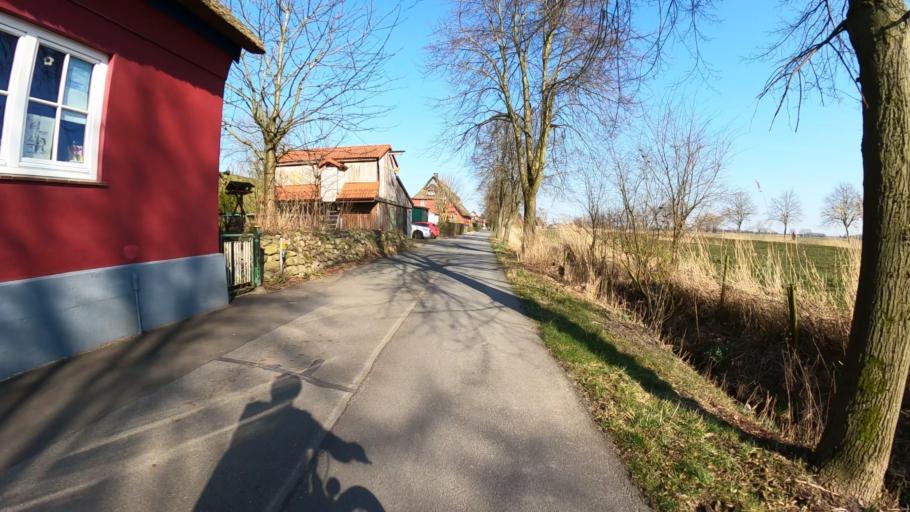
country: DE
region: Schleswig-Holstein
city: Seestermuhe
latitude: 53.7139
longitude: 9.5590
